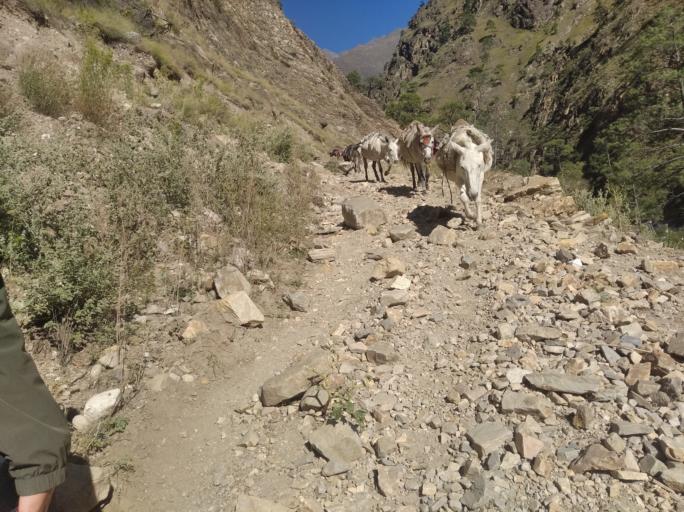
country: NP
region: Western Region
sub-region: Dhawalagiri Zone
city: Jomsom
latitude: 28.9370
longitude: 82.9306
